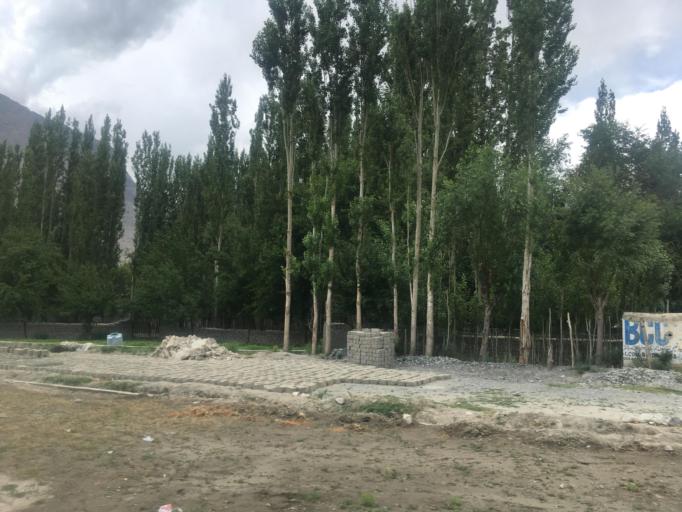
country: PK
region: Gilgit-Baltistan
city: Skardu
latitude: 35.2911
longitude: 75.6154
